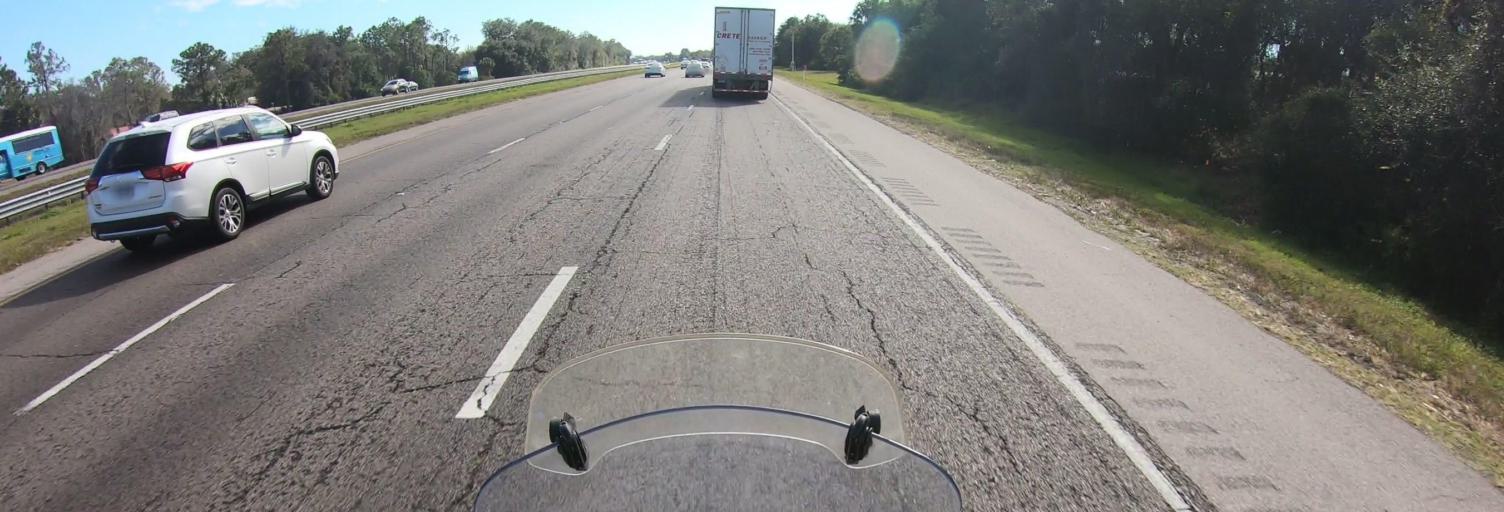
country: US
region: Florida
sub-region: Hillsborough County
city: Gibsonton
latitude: 27.8280
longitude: -82.3513
